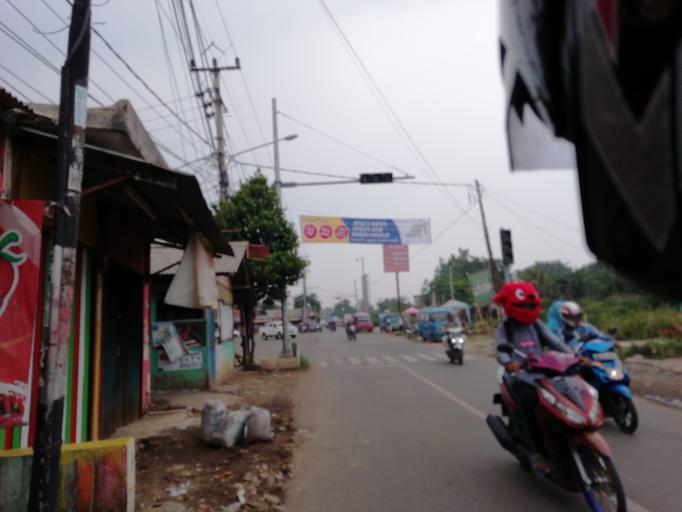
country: ID
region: West Java
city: Cibinong
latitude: -6.4793
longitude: 106.8036
